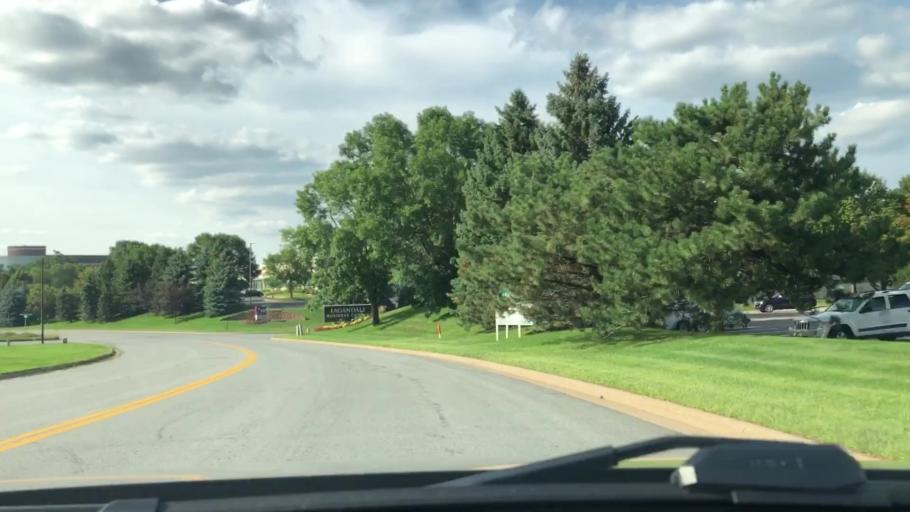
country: US
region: Minnesota
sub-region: Dakota County
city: Mendota Heights
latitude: 44.8565
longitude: -93.1606
